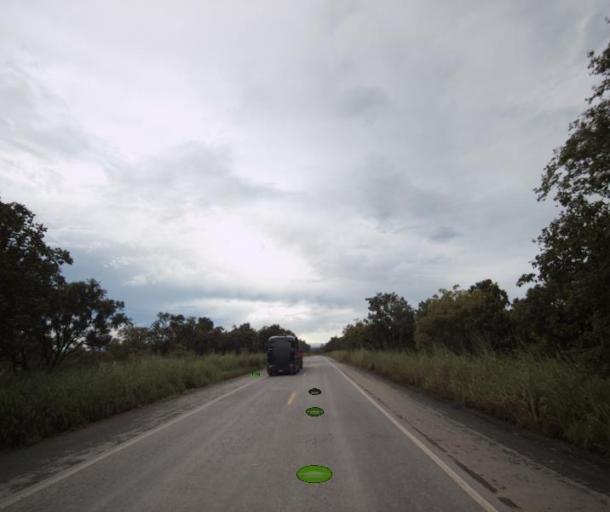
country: BR
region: Goias
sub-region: Porangatu
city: Porangatu
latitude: -13.5425
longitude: -49.1045
